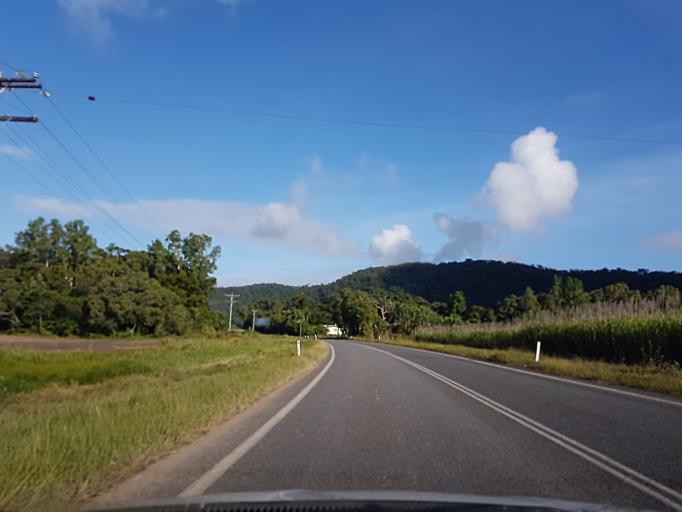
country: AU
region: Queensland
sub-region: Cairns
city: Port Douglas
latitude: -16.3035
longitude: 145.3897
